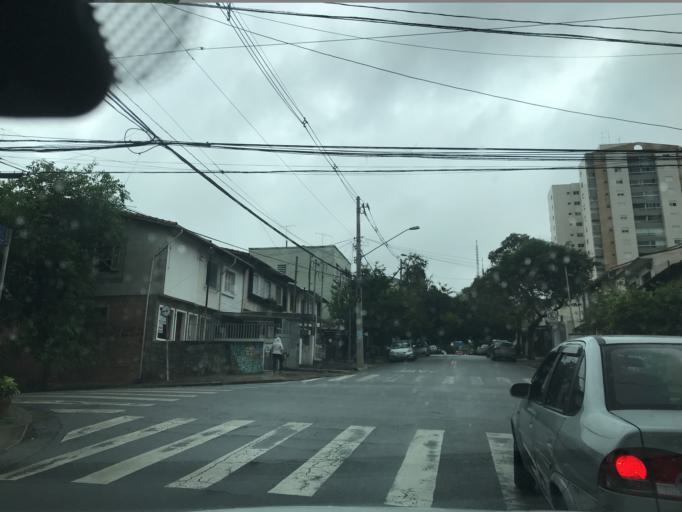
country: BR
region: Sao Paulo
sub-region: Sao Paulo
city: Sao Paulo
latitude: -23.5386
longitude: -46.6769
